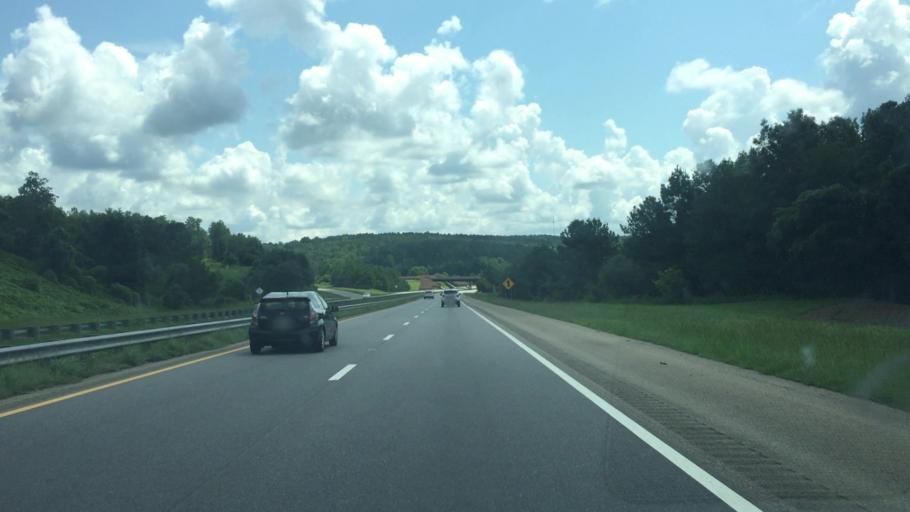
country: US
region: North Carolina
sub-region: Richmond County
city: Cordova
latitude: 34.9473
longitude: -79.8581
